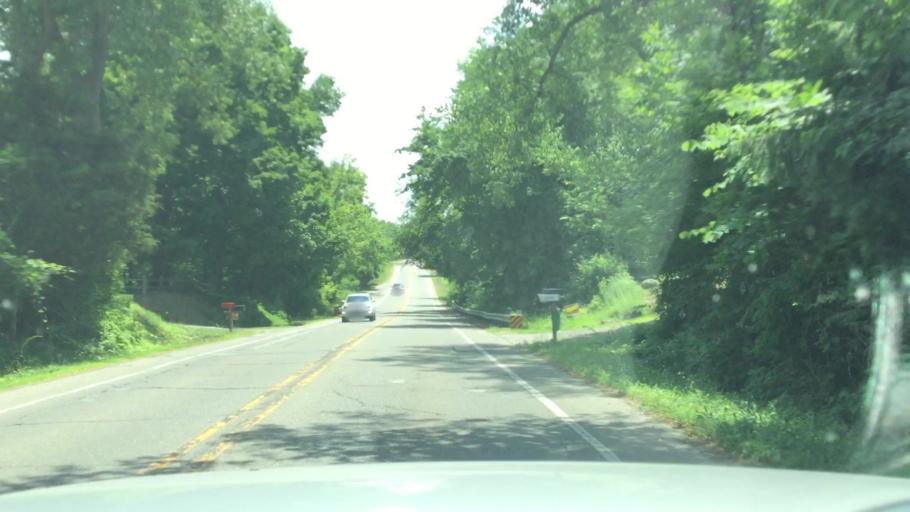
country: US
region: Michigan
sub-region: Genesee County
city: Flushing
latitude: 43.0663
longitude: -83.8661
